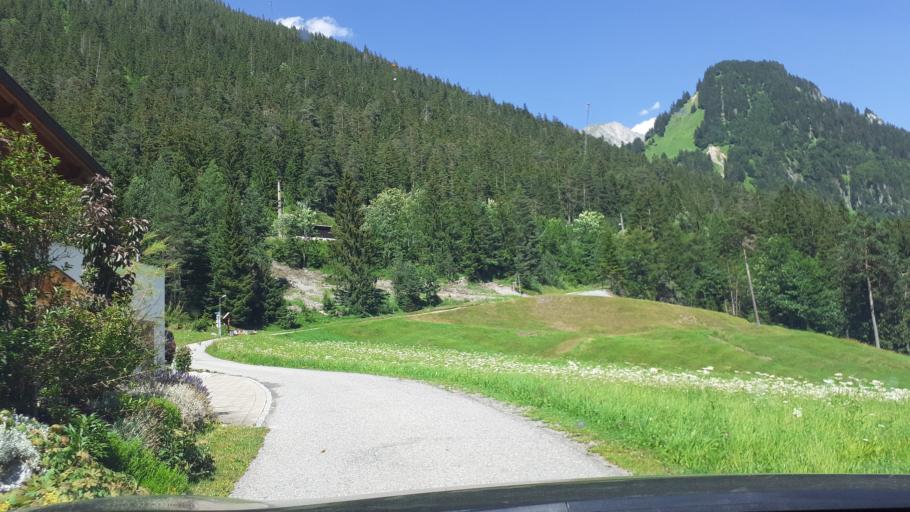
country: AT
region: Vorarlberg
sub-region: Politischer Bezirk Bludenz
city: Klosterle
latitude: 47.1331
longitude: 10.0498
